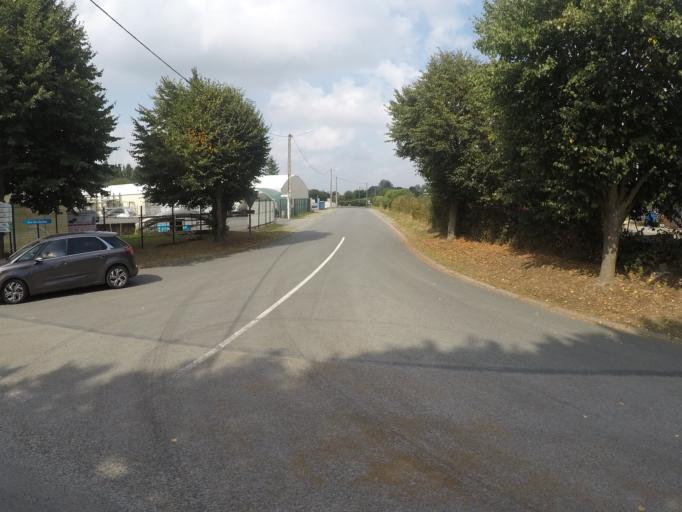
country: FR
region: Brittany
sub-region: Departement des Cotes-d'Armor
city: Plelo
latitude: 48.5326
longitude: -2.9426
